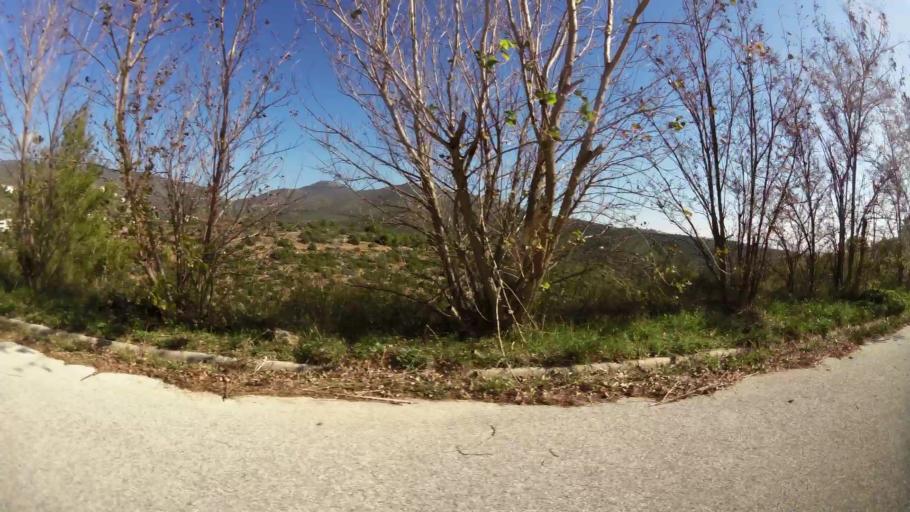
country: GR
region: Attica
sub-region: Nomarchia Anatolikis Attikis
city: Dhrafi
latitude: 38.0291
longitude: 23.9015
